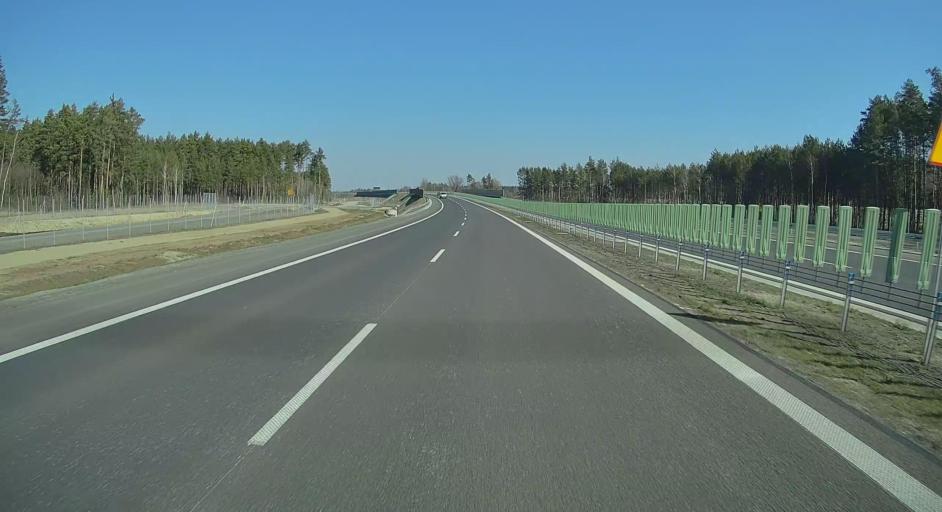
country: PL
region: Subcarpathian Voivodeship
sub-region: Powiat nizanski
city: Raclawice
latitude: 50.4786
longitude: 22.1832
